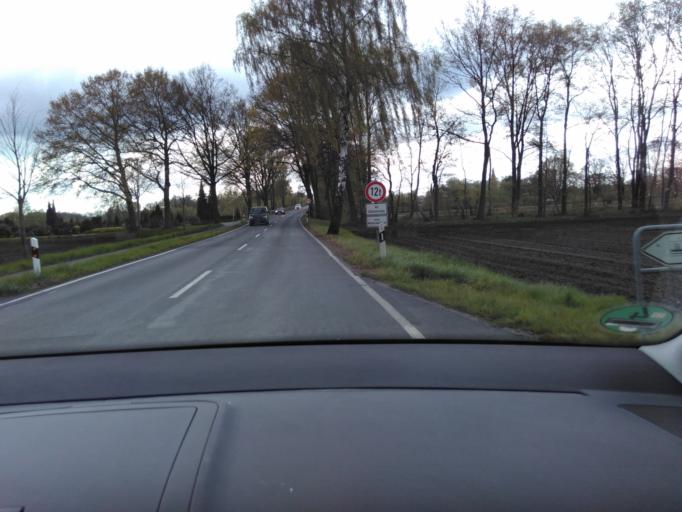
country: DE
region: North Rhine-Westphalia
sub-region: Regierungsbezirk Detmold
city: Verl
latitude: 51.8960
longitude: 8.4708
